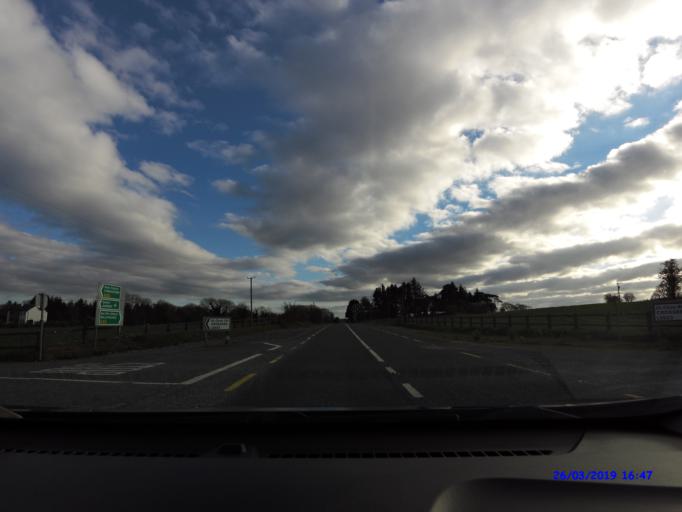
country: IE
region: Connaught
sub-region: Maigh Eo
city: Ballyhaunis
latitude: 53.8150
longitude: -8.7645
